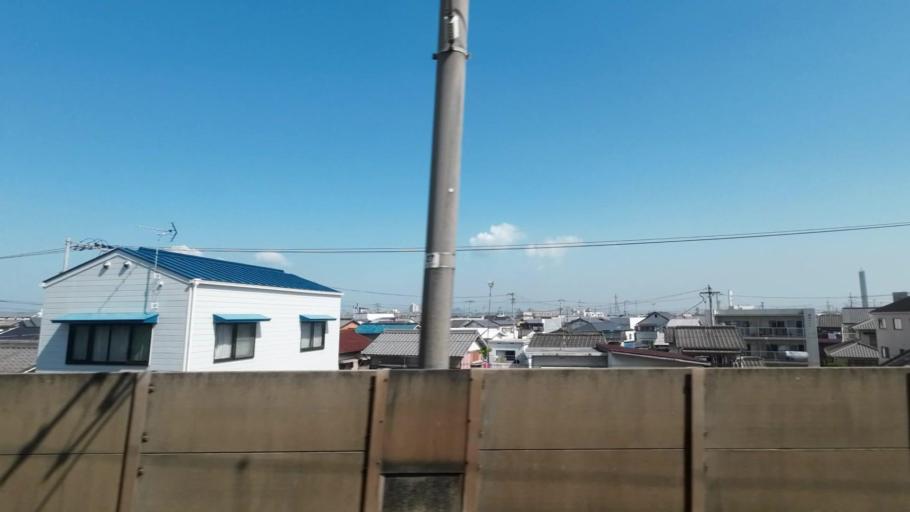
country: JP
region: Kagawa
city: Marugame
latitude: 34.2953
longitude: 133.8018
